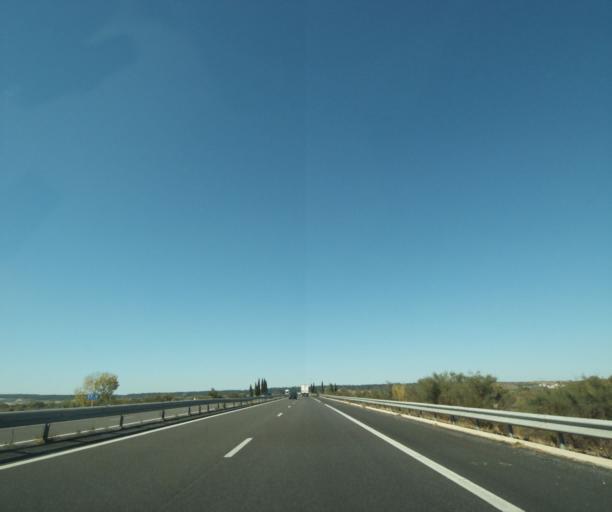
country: FR
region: Languedoc-Roussillon
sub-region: Departement du Gard
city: Bellegarde
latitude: 43.7238
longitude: 4.5053
